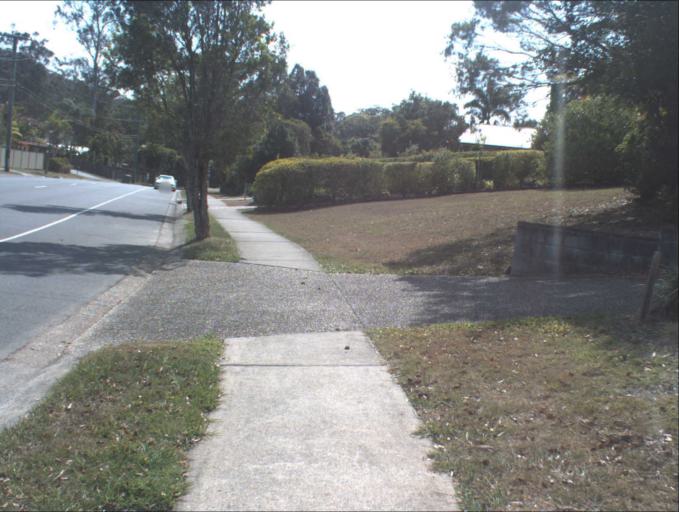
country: AU
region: Queensland
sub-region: Logan
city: Slacks Creek
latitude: -27.6553
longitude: 153.1903
